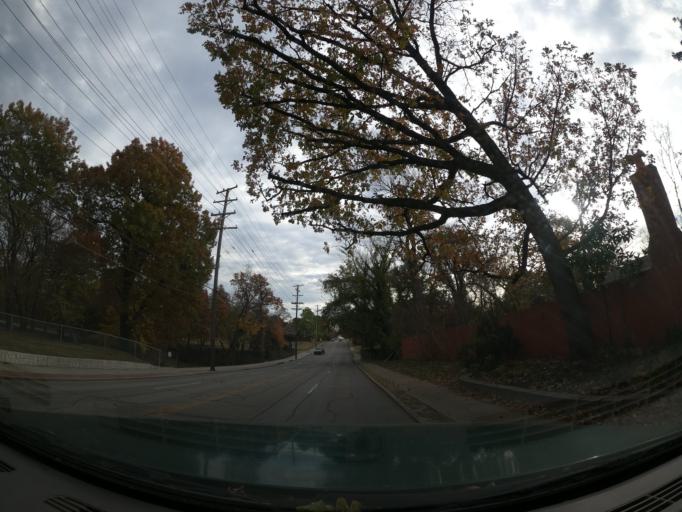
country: US
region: Oklahoma
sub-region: Tulsa County
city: Tulsa
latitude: 36.1259
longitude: -95.9582
